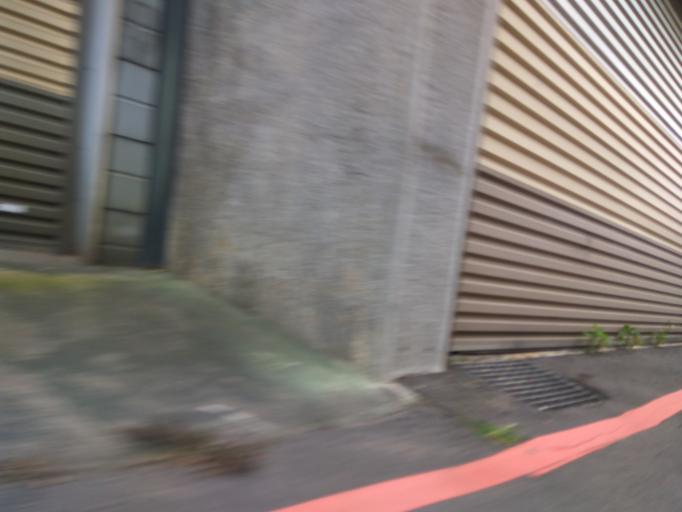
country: TW
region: Taiwan
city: Daxi
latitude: 24.9414
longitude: 121.2038
